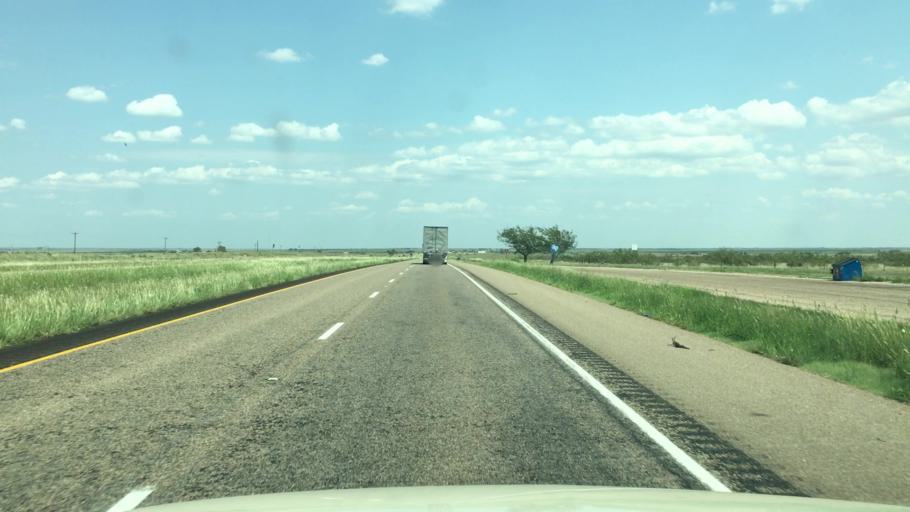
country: US
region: Texas
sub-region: Armstrong County
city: Claude
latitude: 35.0327
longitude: -101.1509
